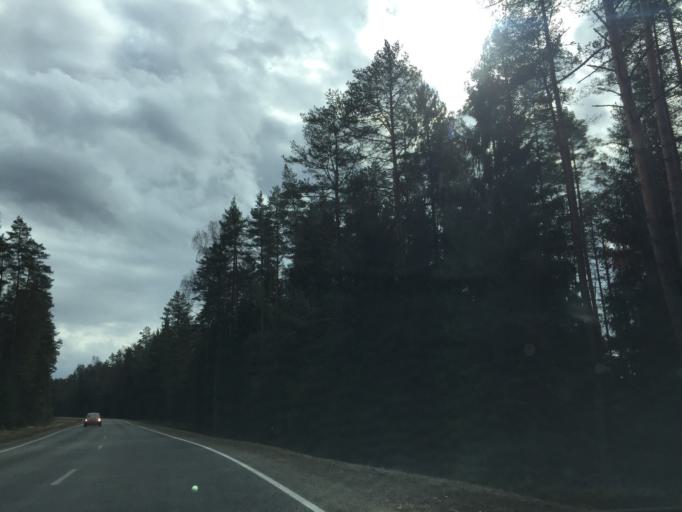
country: LV
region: Incukalns
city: Incukalns
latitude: 57.0608
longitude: 24.6676
